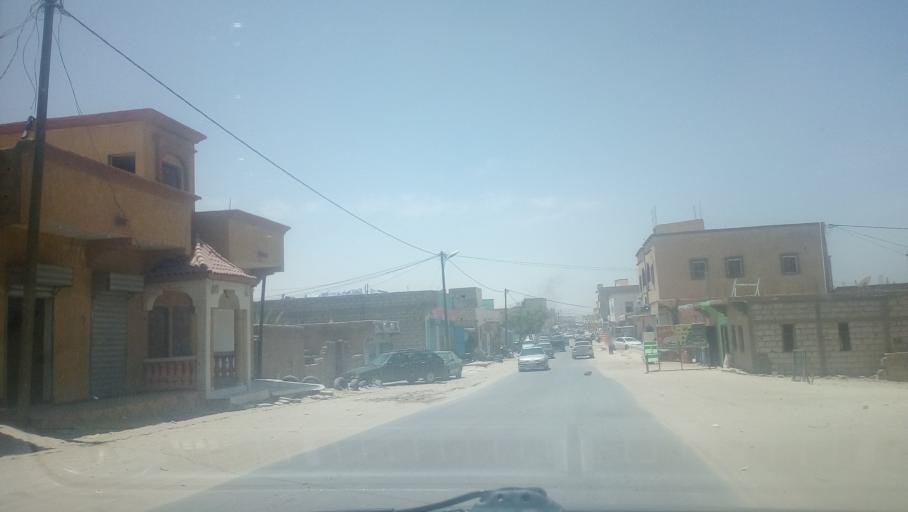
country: MR
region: Nouakchott
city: Nouakchott
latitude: 18.0593
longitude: -15.9608
